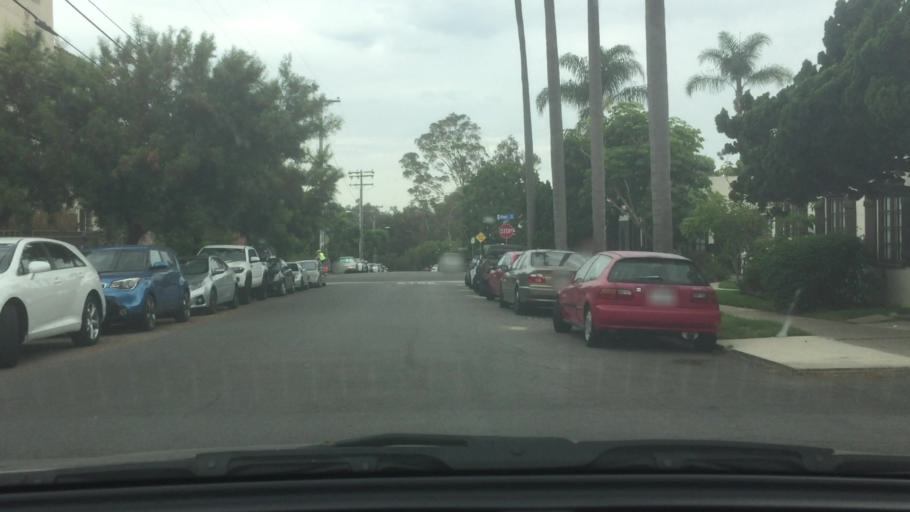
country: US
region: California
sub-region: San Diego County
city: San Diego
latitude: 32.7452
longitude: -117.1632
